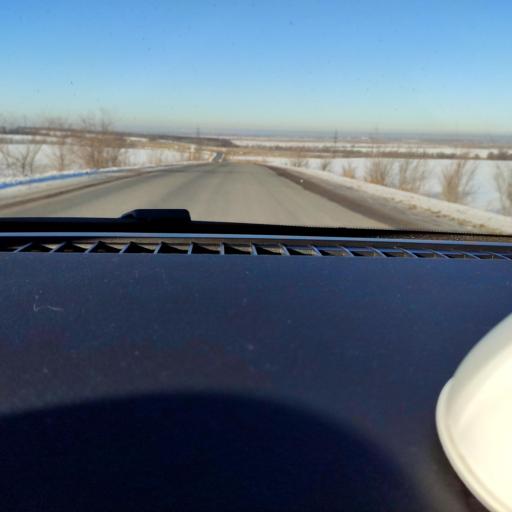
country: RU
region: Samara
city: Kinel'
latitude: 53.1451
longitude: 50.5210
